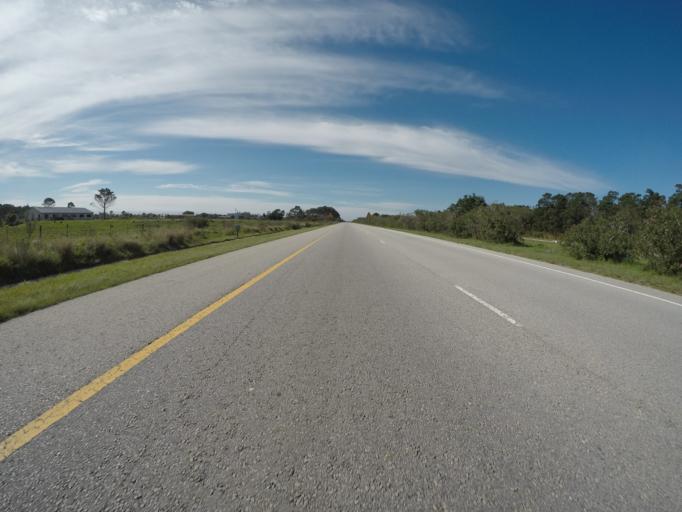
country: ZA
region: Eastern Cape
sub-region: Nelson Mandela Bay Metropolitan Municipality
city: Uitenhage
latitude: -33.9210
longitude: 25.3023
